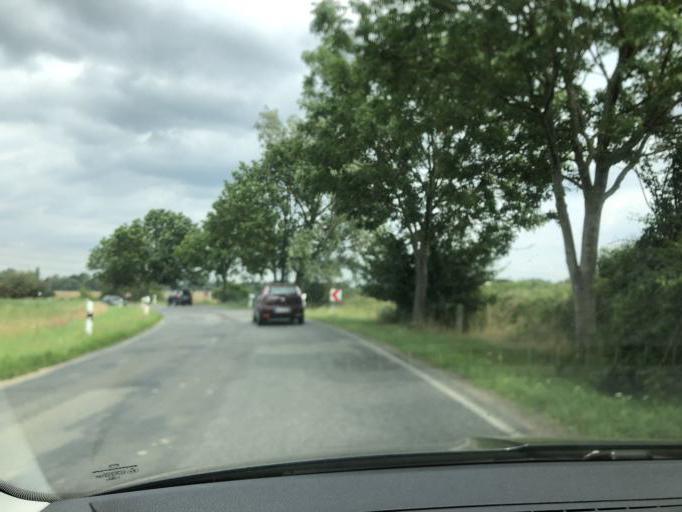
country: DE
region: Mecklenburg-Vorpommern
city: Klein Rogahn
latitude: 53.6002
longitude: 11.3581
